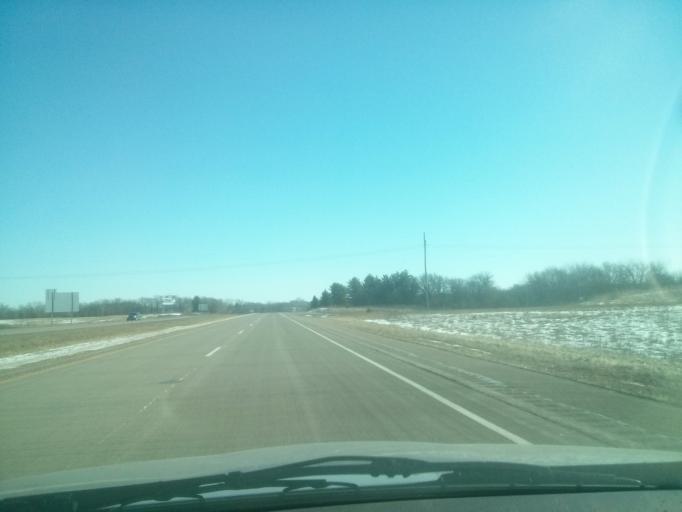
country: US
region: Wisconsin
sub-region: Saint Croix County
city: Somerset
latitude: 45.1216
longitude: -92.6525
